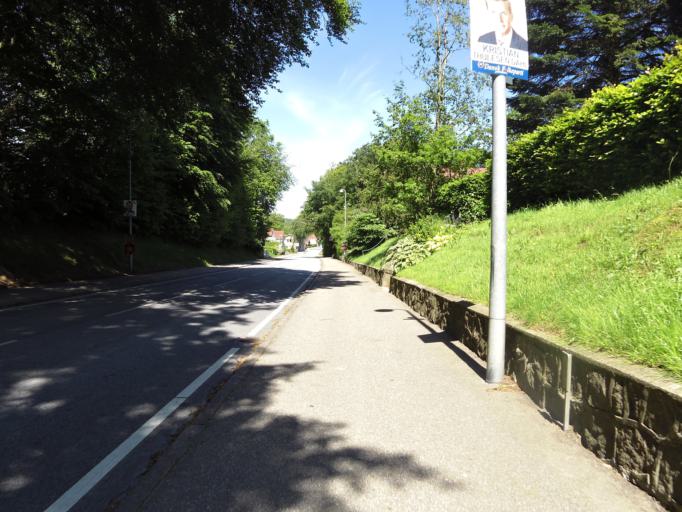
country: DK
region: South Denmark
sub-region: Haderslev Kommune
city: Gram
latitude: 55.2923
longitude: 9.0534
